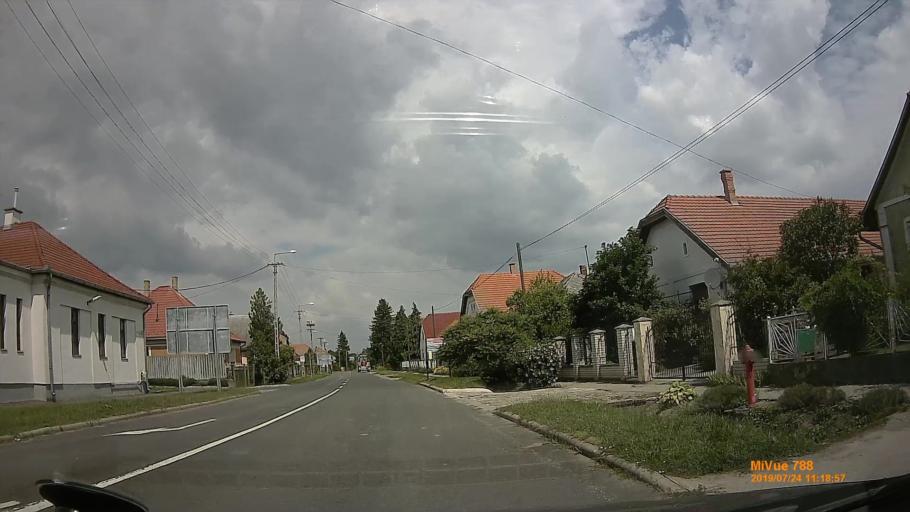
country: HU
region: Szabolcs-Szatmar-Bereg
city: Tarpa
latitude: 48.1609
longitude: 22.4587
